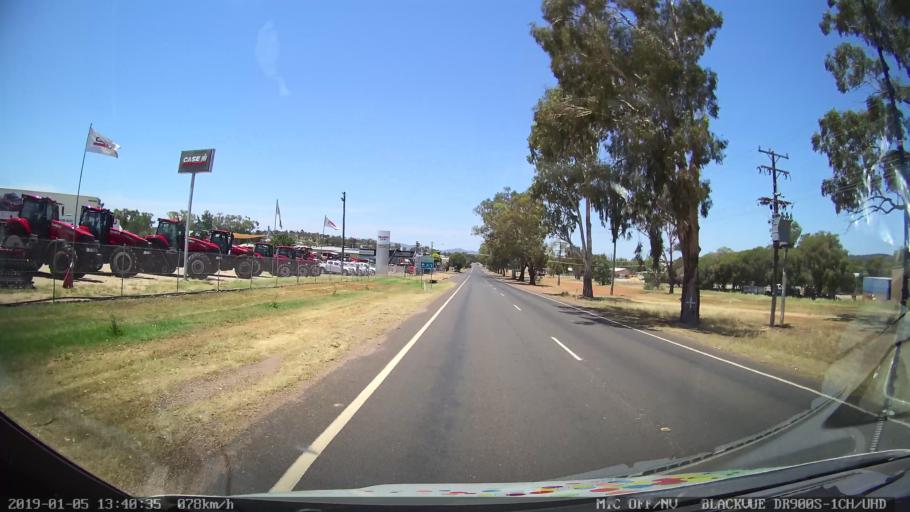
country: AU
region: New South Wales
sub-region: Gunnedah
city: Gunnedah
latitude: -30.9813
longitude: 150.2308
